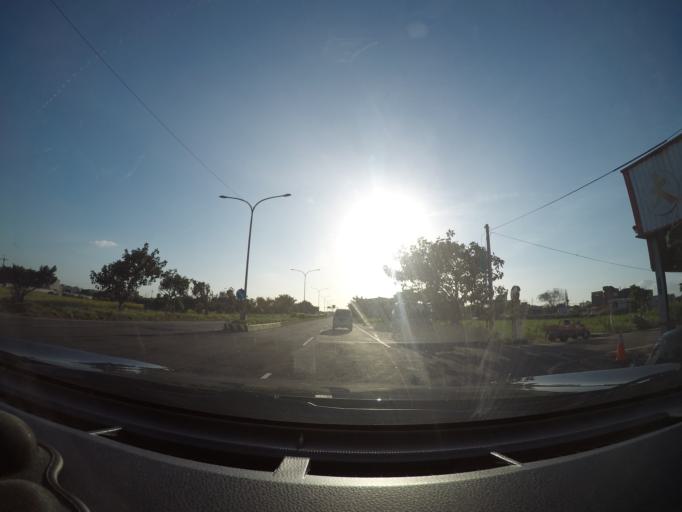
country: TW
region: Taiwan
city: Taoyuan City
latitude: 25.0773
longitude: 121.2060
